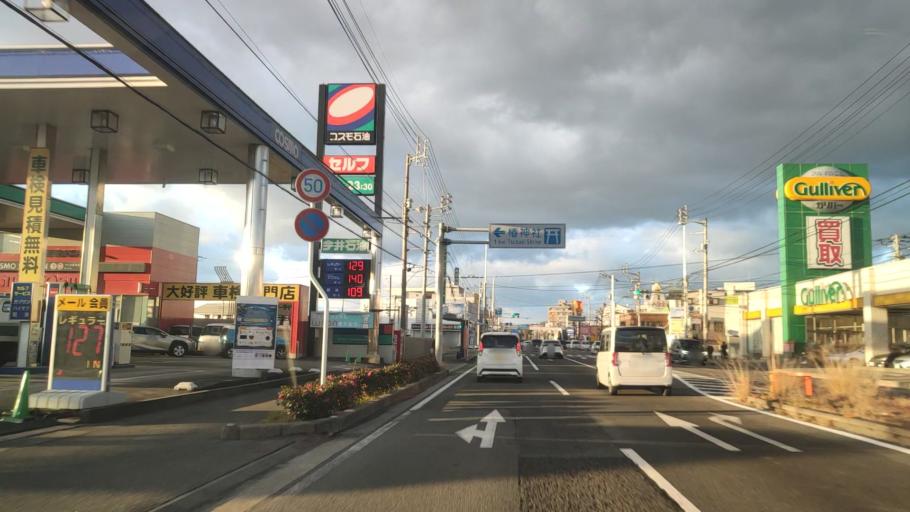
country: JP
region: Ehime
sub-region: Shikoku-chuo Shi
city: Matsuyama
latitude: 33.8085
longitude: 132.7804
